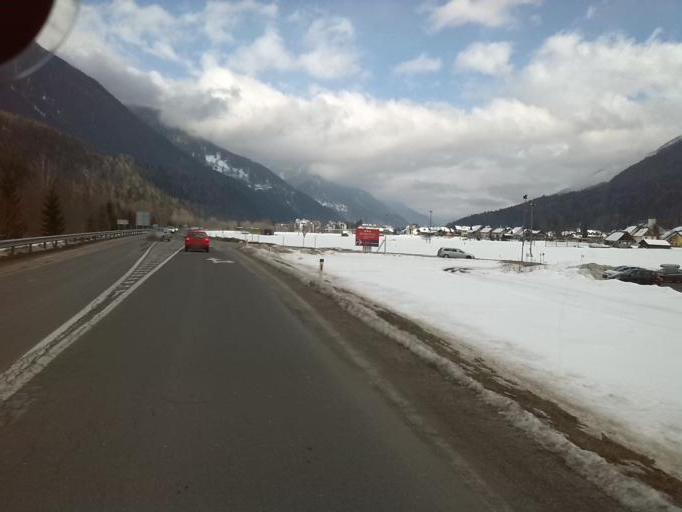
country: SI
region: Kranjska Gora
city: Kranjska Gora
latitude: 46.4879
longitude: 13.7778
